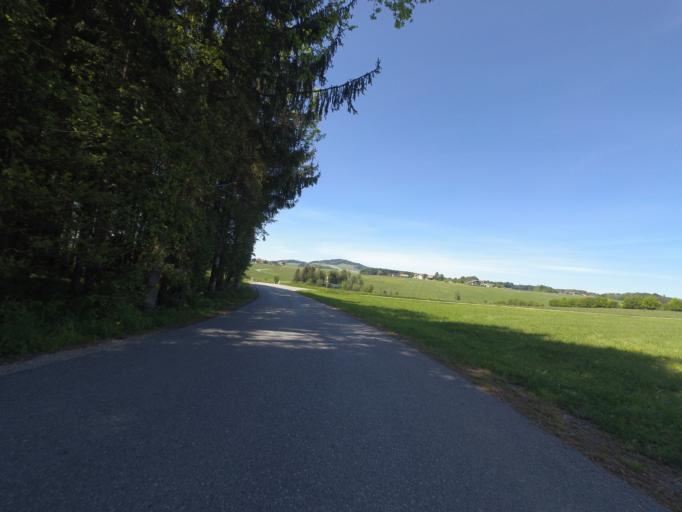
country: AT
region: Salzburg
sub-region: Politischer Bezirk Salzburg-Umgebung
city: Seekirchen am Wallersee
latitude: 47.9205
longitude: 13.1283
